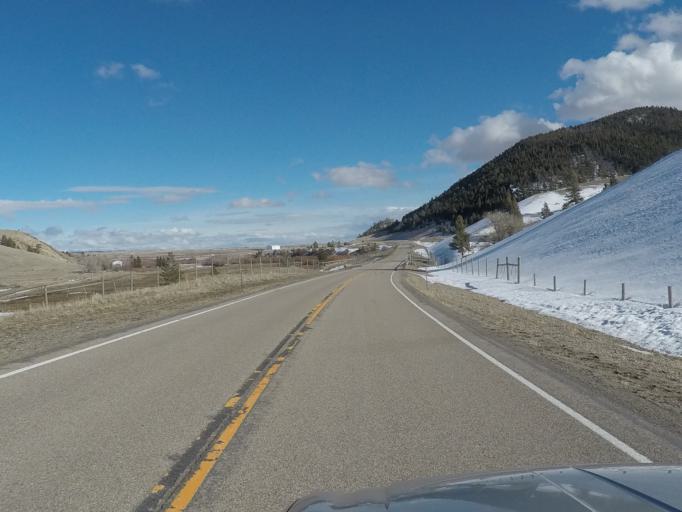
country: US
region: Montana
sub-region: Meagher County
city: White Sulphur Springs
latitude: 46.5437
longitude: -110.4519
